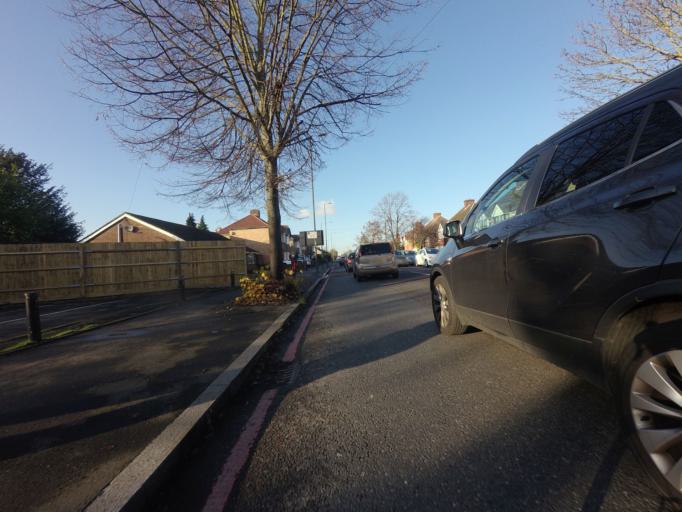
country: GB
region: England
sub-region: Greater London
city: Feltham
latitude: 51.4463
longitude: -0.4009
